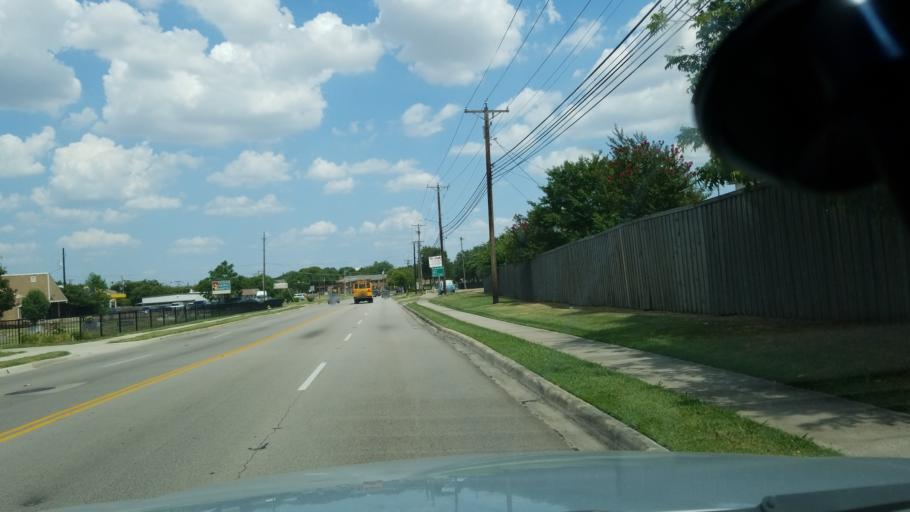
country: US
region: Texas
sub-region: Dallas County
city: Irving
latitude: 32.8284
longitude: -96.9882
